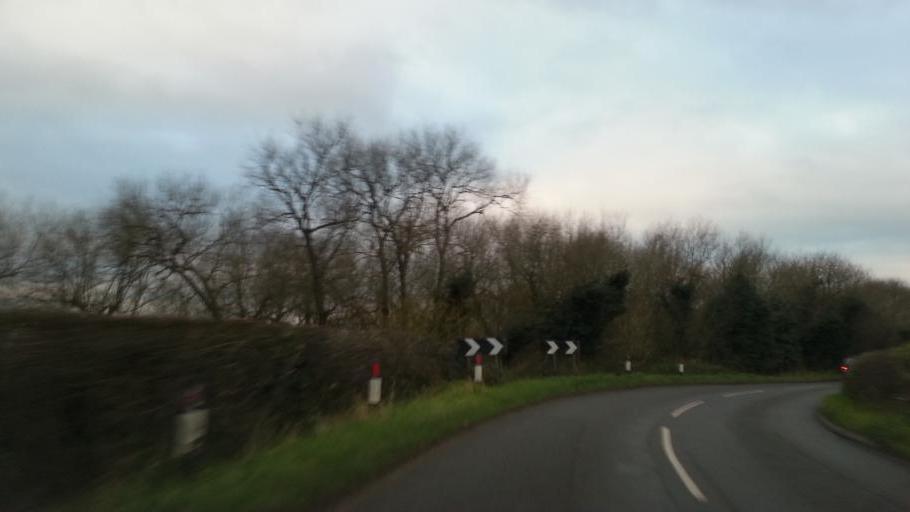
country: GB
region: England
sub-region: Nottinghamshire
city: Newark on Trent
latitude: 53.1009
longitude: -0.8308
